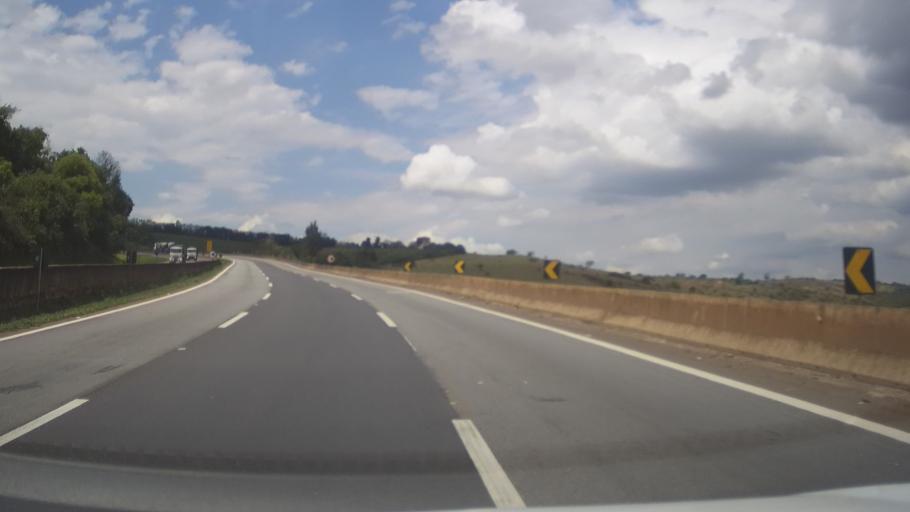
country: BR
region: Minas Gerais
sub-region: Nepomuceno
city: Nepomuceno
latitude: -21.2869
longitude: -45.1418
